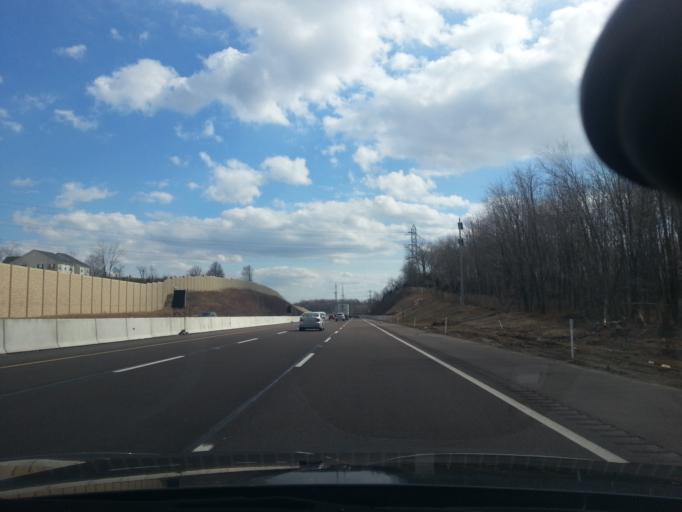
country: US
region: Pennsylvania
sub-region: Montgomery County
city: Blue Bell
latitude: 40.1740
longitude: -75.3076
